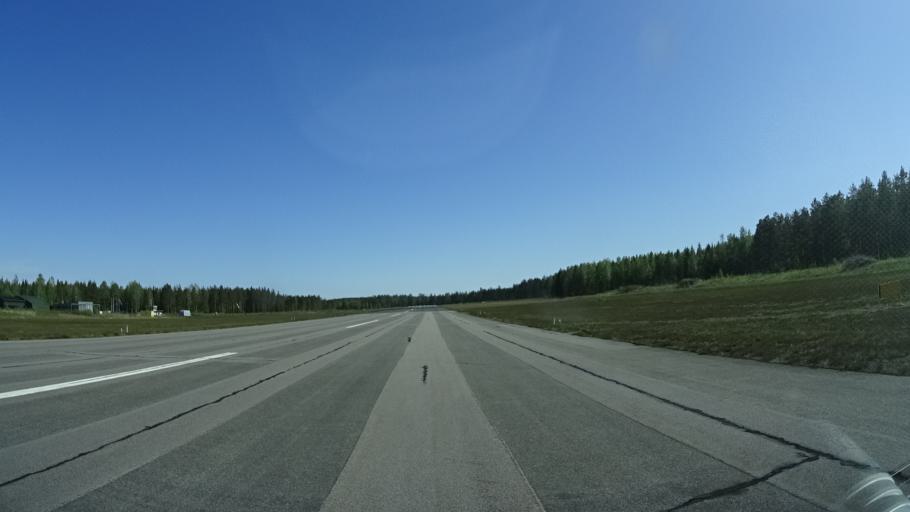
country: SE
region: Kalmar
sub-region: Vasterviks Kommun
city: Vaestervik
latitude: 57.7786
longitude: 16.5251
